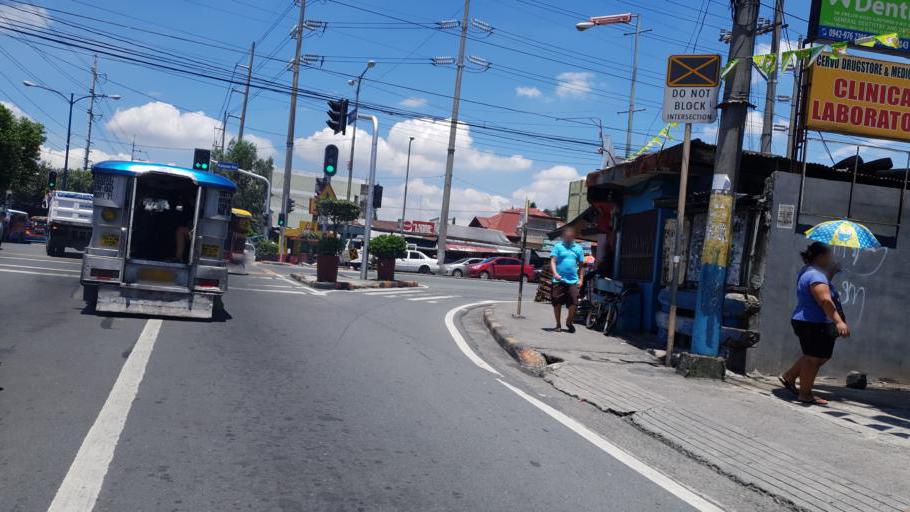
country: PH
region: Calabarzon
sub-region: Province of Rizal
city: Pateros
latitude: 14.5548
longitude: 121.0644
